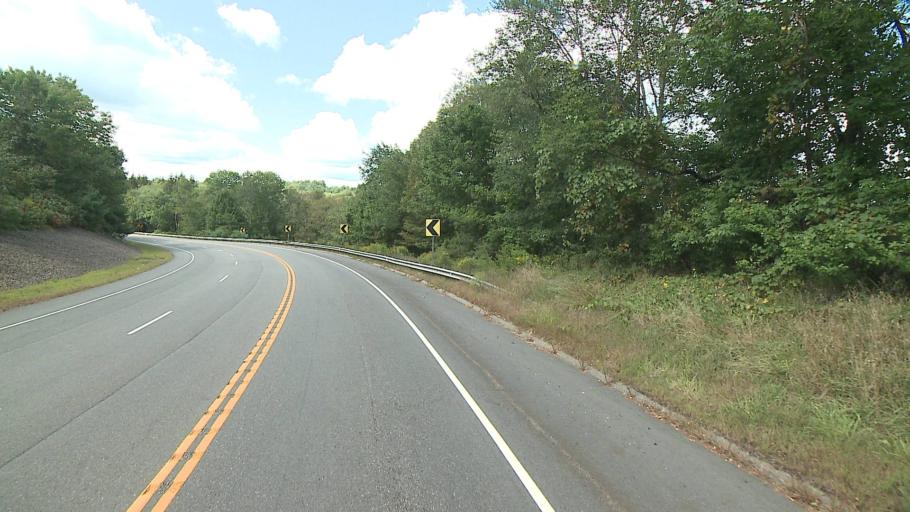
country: US
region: Connecticut
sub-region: Windham County
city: South Woodstock
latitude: 41.8789
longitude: -72.0811
